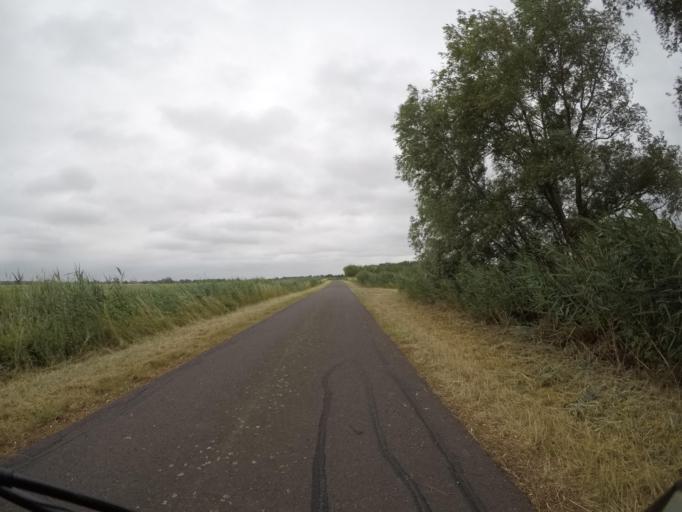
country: DE
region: Lower Saxony
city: Hitzacker
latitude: 53.1656
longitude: 11.0917
